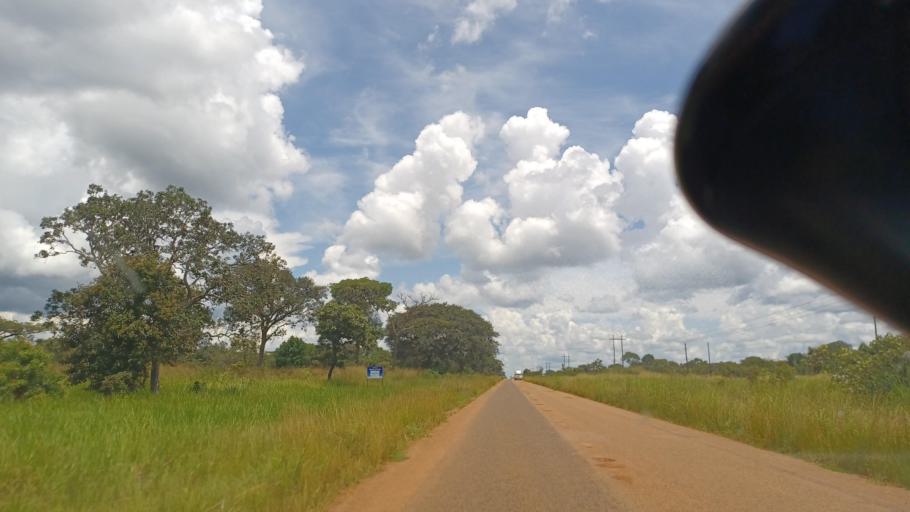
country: ZM
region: North-Western
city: Solwezi
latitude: -12.4892
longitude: 26.1913
